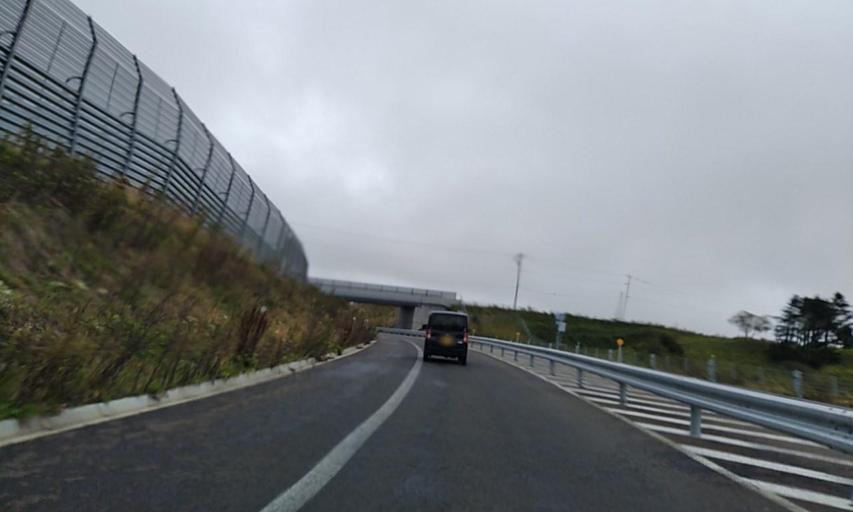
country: JP
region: Hokkaido
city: Nemuro
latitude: 43.2748
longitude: 145.5067
